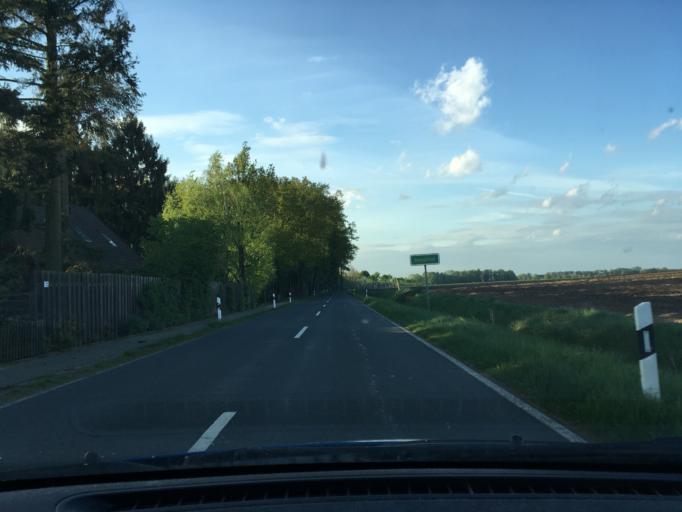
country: DE
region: Lower Saxony
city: Wietzendorf
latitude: 52.8974
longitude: 9.9837
